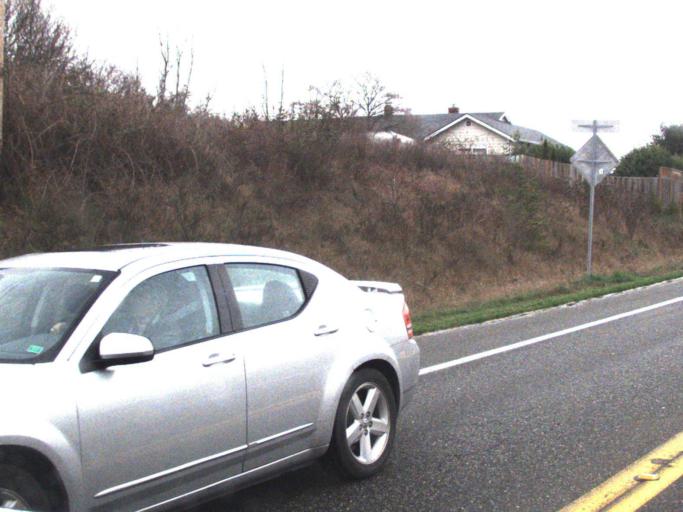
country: US
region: Washington
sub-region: Snohomish County
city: Stanwood
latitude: 48.2413
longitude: -122.4428
